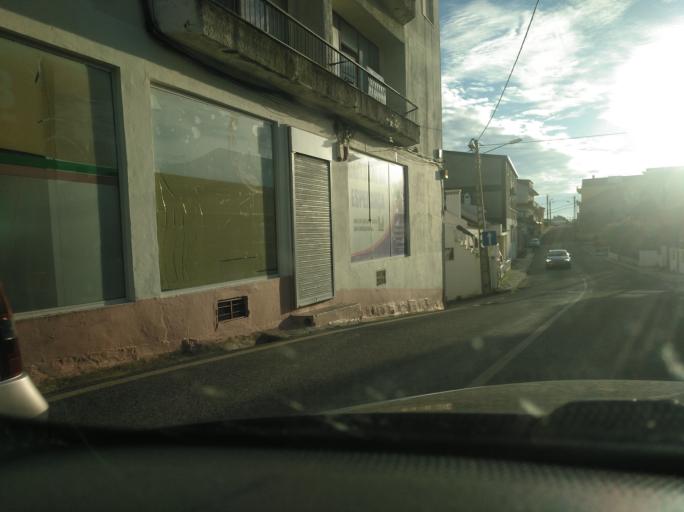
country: PT
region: Lisbon
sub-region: Loures
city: Unhos
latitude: 38.8184
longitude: -9.1213
